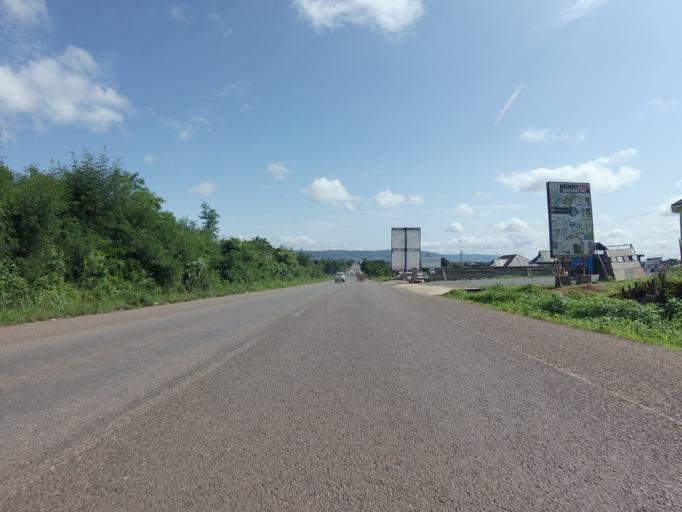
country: GH
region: Eastern
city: Aburi
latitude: 5.8272
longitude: -0.1189
